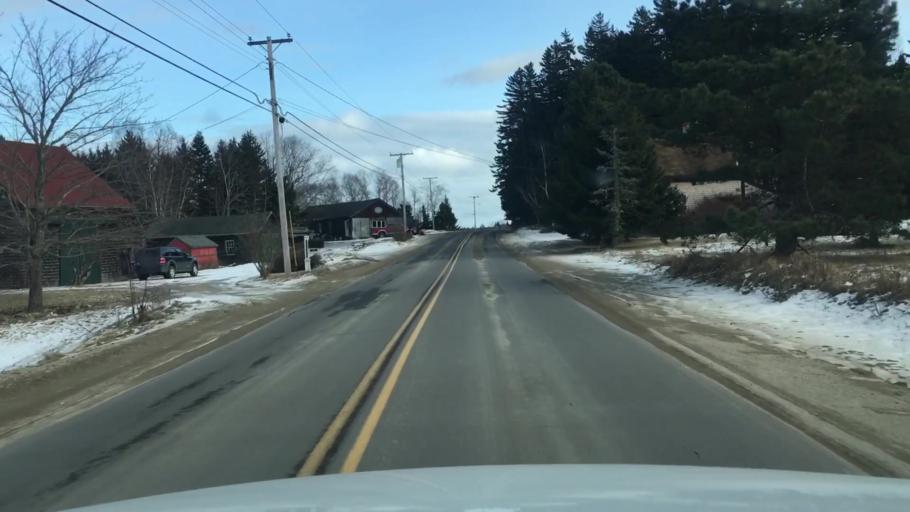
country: US
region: Maine
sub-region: Washington County
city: Jonesport
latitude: 44.6088
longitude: -67.5999
